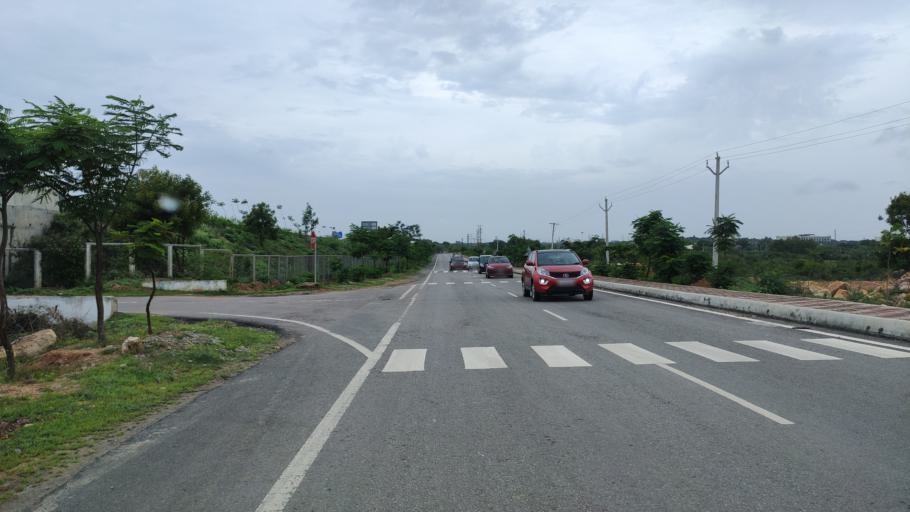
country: IN
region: Telangana
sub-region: Rangareddi
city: Secunderabad
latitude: 17.5788
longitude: 78.5814
